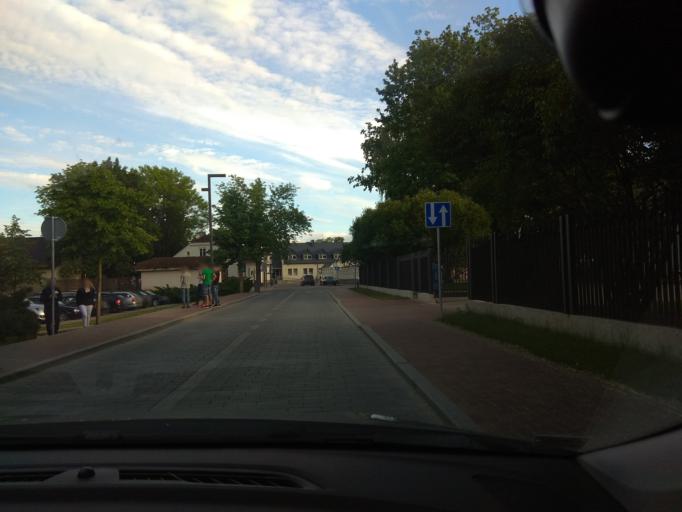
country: LT
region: Marijampoles apskritis
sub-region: Marijampole Municipality
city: Marijampole
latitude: 54.5561
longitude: 23.3452
